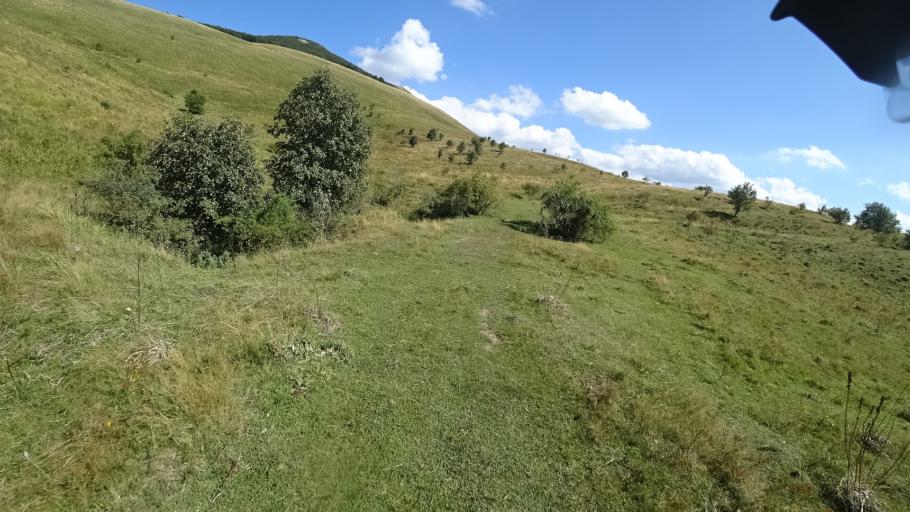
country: HR
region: Zadarska
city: Gracac
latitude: 44.4086
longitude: 16.0026
